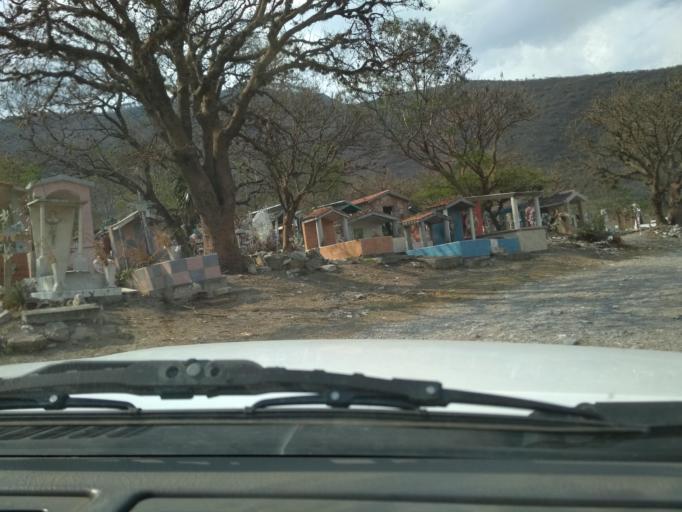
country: MX
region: Veracruz
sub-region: Acultzingo
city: Sierra de Agua
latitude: 18.7697
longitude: -97.2306
